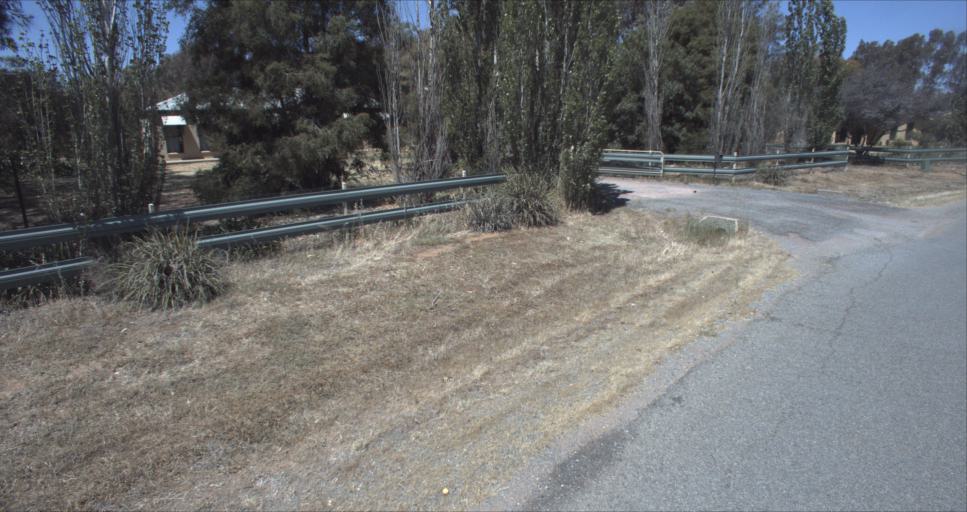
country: AU
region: New South Wales
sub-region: Leeton
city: Leeton
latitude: -34.5294
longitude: 146.3985
